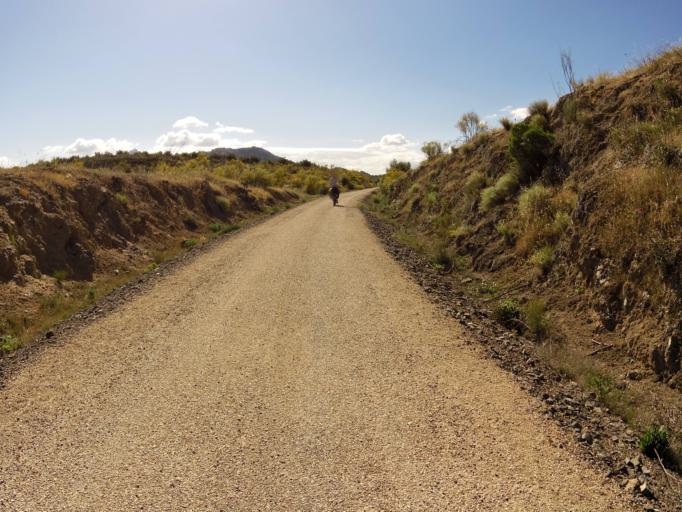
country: ES
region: Andalusia
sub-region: Provincia de Jaen
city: Alcaudete
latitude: 37.6052
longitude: -4.1541
